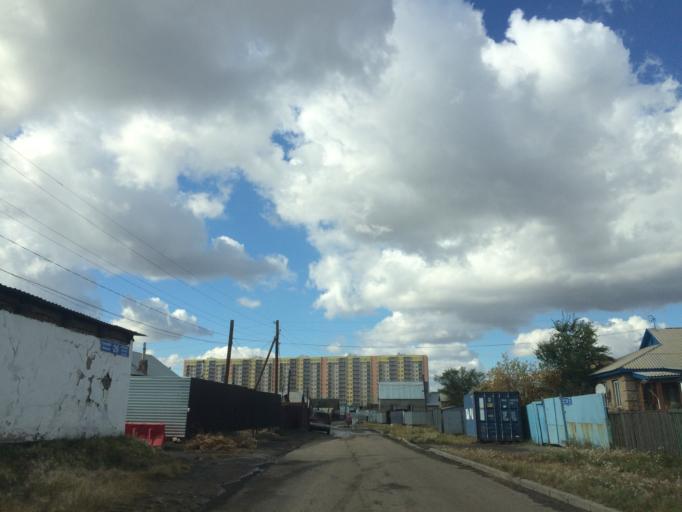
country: KZ
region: Astana Qalasy
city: Astana
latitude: 51.1873
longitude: 71.3887
